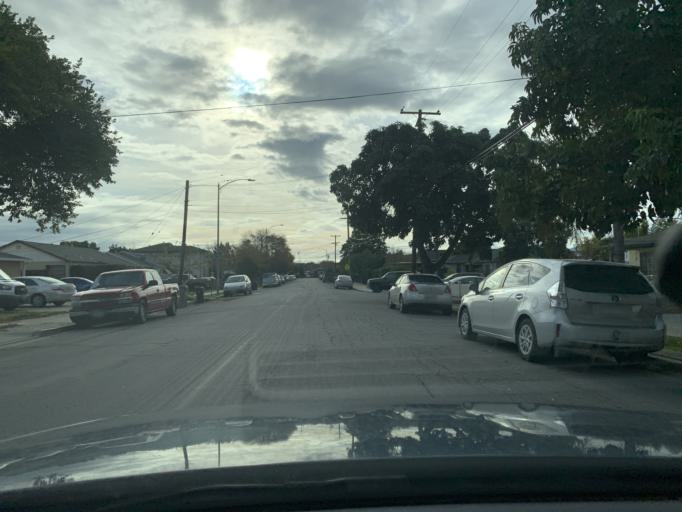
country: US
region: California
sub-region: Santa Clara County
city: Alum Rock
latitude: 37.3504
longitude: -121.8480
